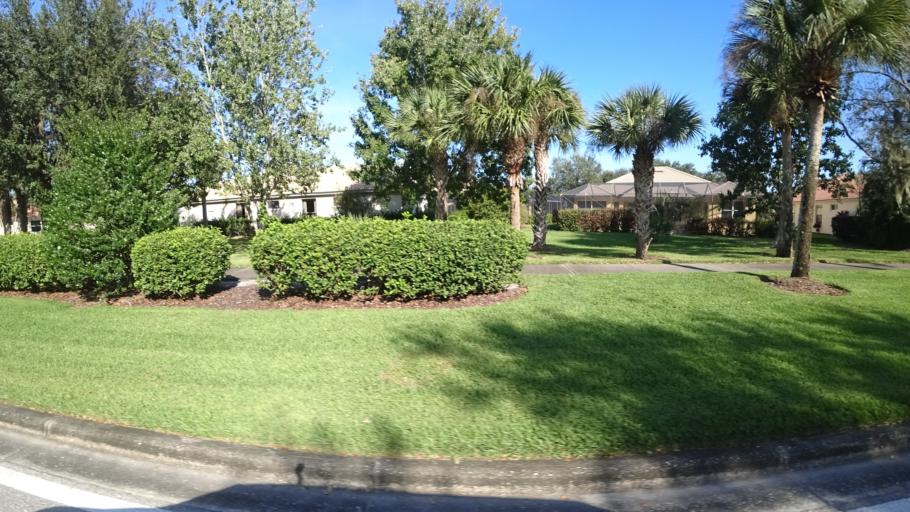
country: US
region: Florida
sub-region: Sarasota County
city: Desoto Lakes
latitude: 27.4212
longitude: -82.4648
